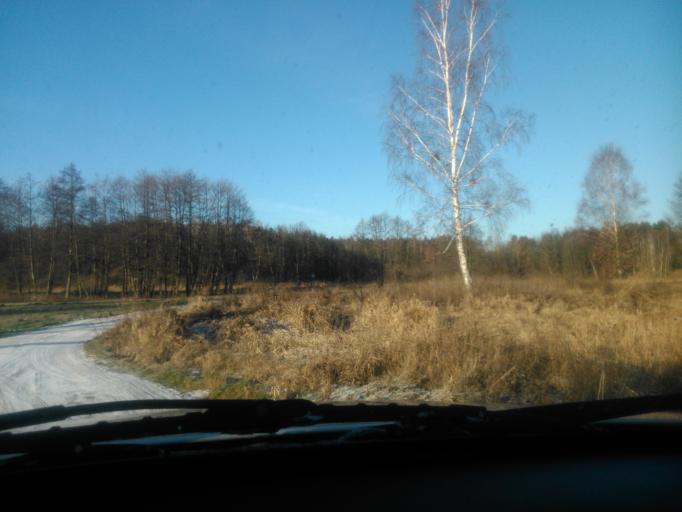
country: PL
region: Warmian-Masurian Voivodeship
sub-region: Powiat nowomiejski
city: Kurzetnik
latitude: 53.3677
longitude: 19.5250
